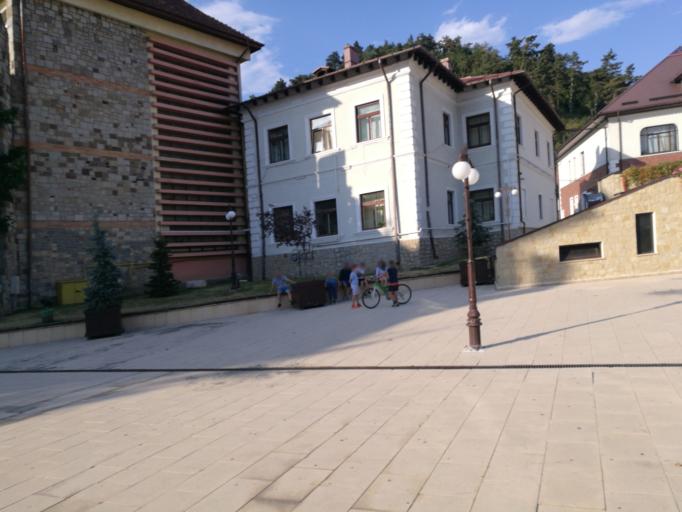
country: RO
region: Neamt
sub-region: Municipiul Piatra-Neamt
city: Valeni
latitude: 46.9333
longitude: 26.3689
